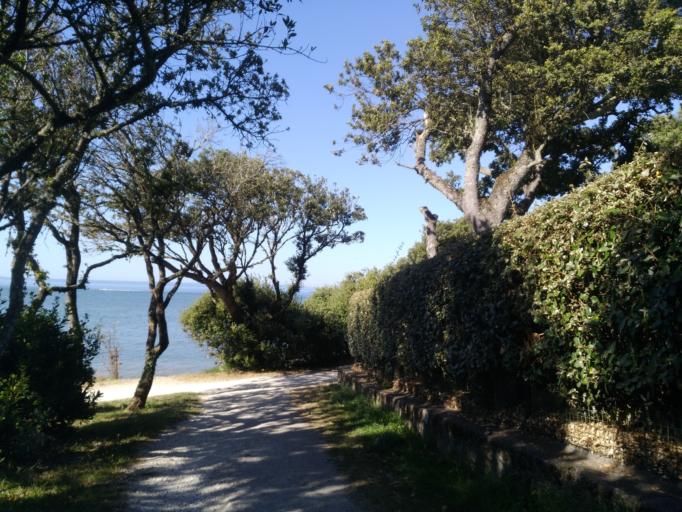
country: FR
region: Poitou-Charentes
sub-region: Departement de la Charente-Maritime
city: Saint-Palais-sur-Mer
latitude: 45.6402
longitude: -1.0920
